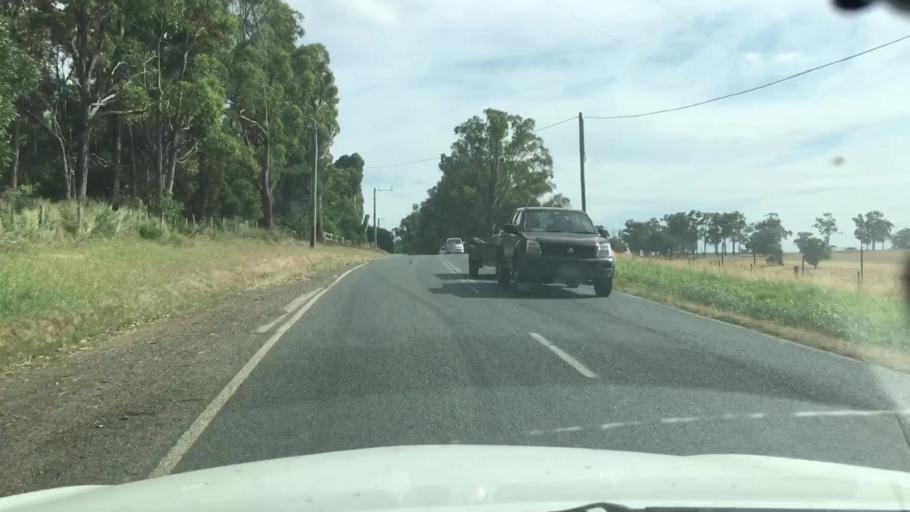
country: AU
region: Victoria
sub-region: Yarra Ranges
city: Macclesfield
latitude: -37.8721
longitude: 145.4788
